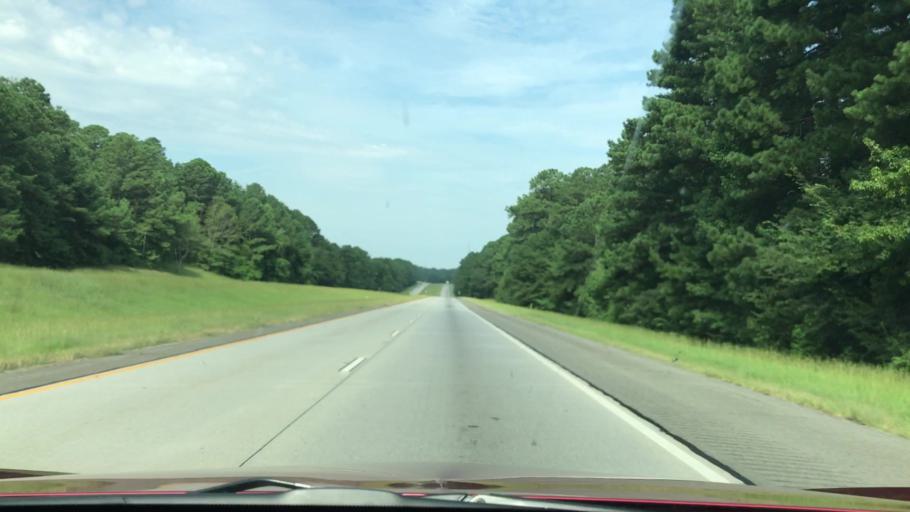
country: US
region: Georgia
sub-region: Warren County
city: Firing Range
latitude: 33.5044
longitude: -82.7532
